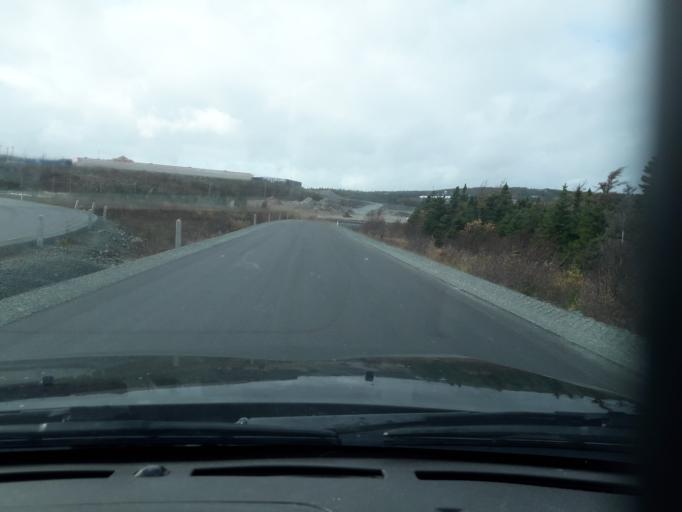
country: CA
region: Newfoundland and Labrador
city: Mount Pearl
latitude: 47.5560
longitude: -52.7742
